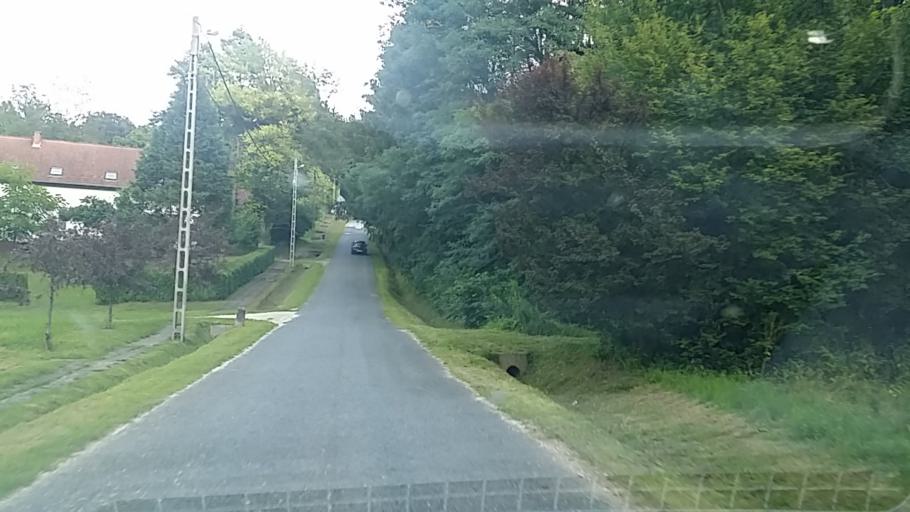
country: HU
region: Zala
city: Becsehely
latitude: 46.5207
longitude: 16.7295
